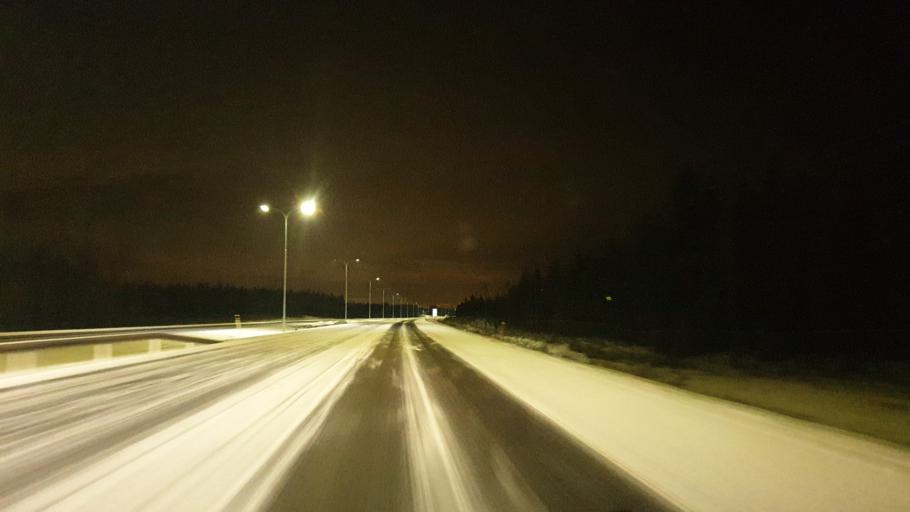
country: FI
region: Northern Ostrobothnia
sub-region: Oulu
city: Haukipudas
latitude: 65.1429
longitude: 25.4328
